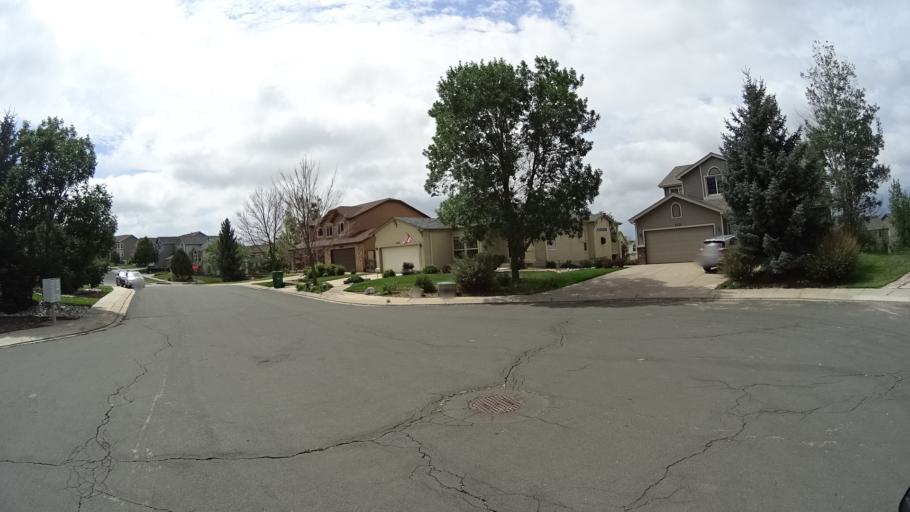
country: US
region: Colorado
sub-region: El Paso County
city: Gleneagle
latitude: 39.0108
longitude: -104.8025
